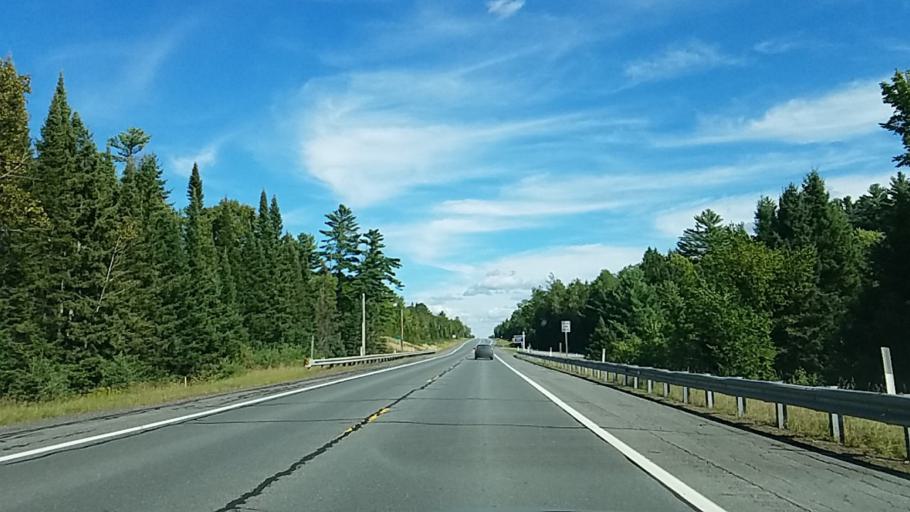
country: US
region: Michigan
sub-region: Baraga County
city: L'Anse
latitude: 46.5755
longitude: -88.3419
